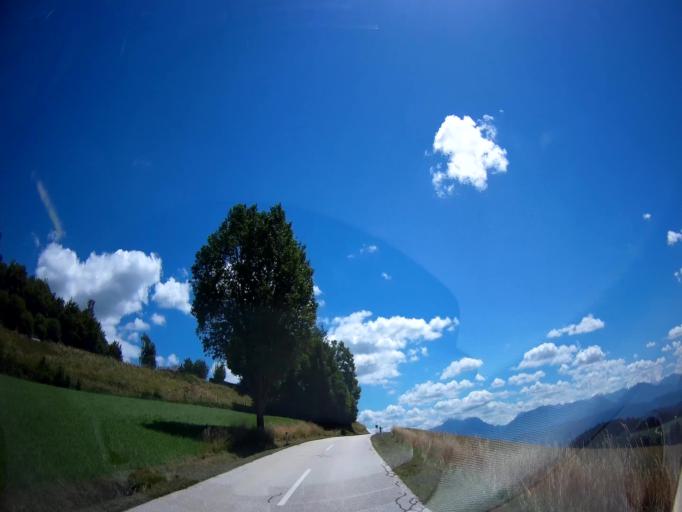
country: AT
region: Carinthia
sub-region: Politischer Bezirk Sankt Veit an der Glan
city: St. Georgen am Laengsee
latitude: 46.7207
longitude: 14.4219
